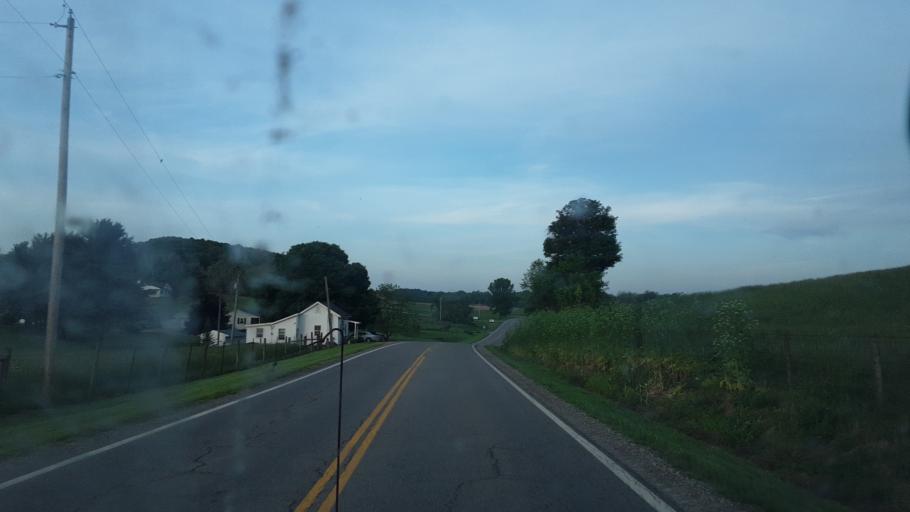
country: US
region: Ohio
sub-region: Ross County
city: Kingston
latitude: 39.4580
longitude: -82.7675
